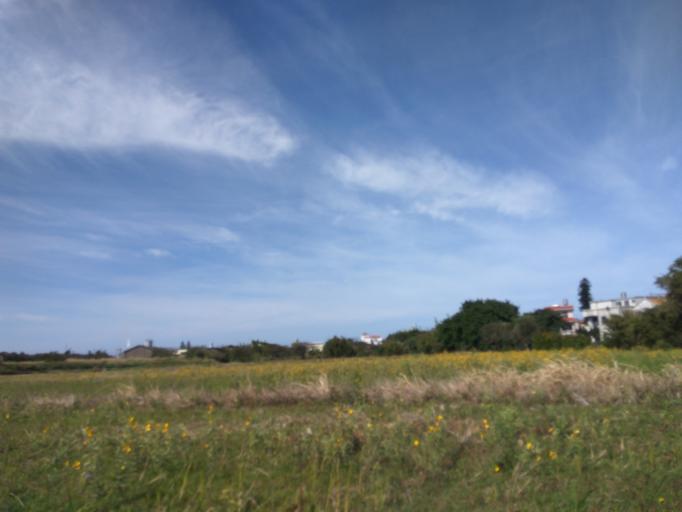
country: TW
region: Taiwan
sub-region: Hsinchu
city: Zhubei
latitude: 25.0213
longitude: 121.0636
